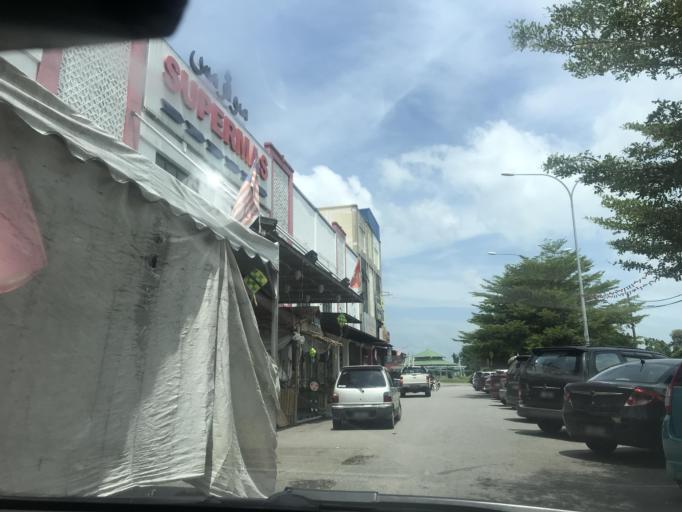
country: MY
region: Kelantan
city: Tumpat
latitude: 6.1658
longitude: 102.1897
